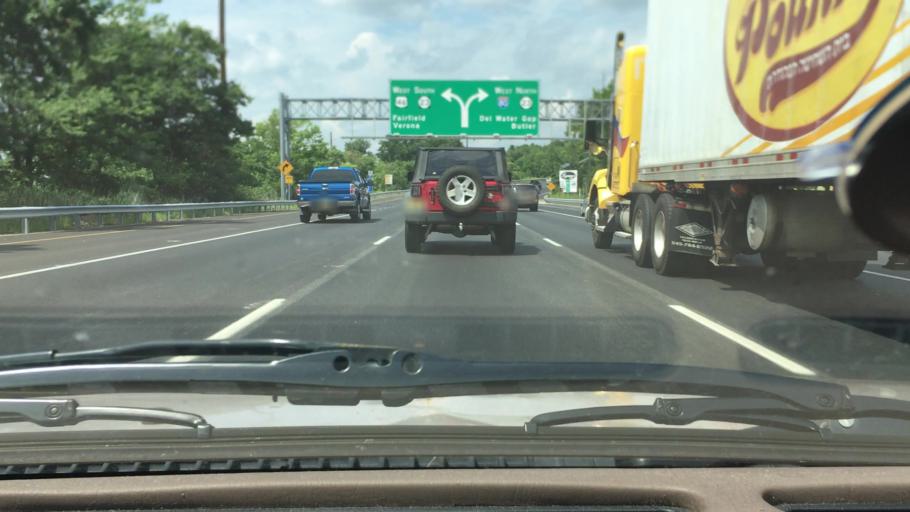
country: US
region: New Jersey
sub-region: Passaic County
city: Singac
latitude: 40.8949
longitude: -74.2447
